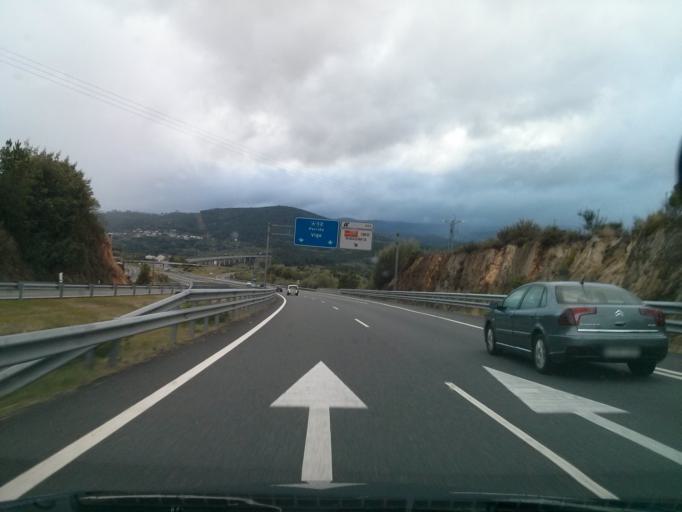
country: ES
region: Galicia
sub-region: Provincia de Ourense
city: Beade
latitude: 42.3084
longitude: -8.1150
